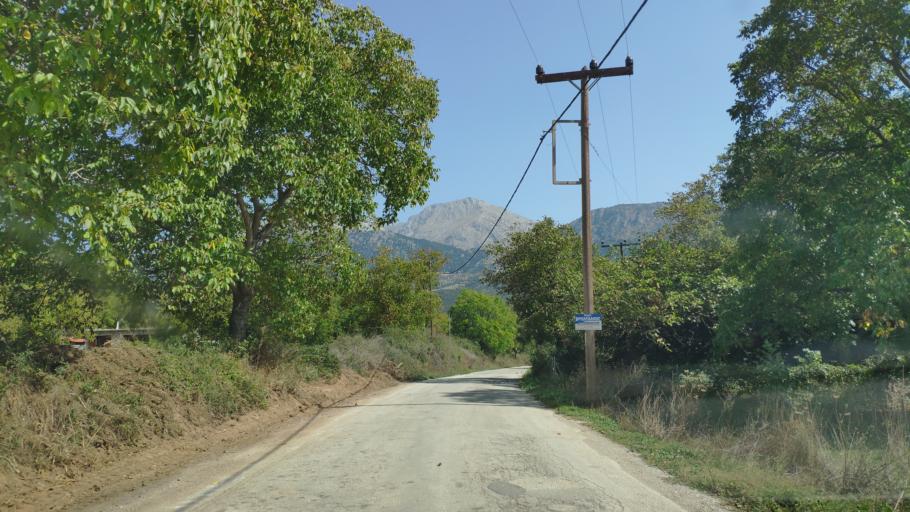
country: GR
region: West Greece
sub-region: Nomos Achaias
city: Kalavryta
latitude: 37.9131
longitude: 22.3046
